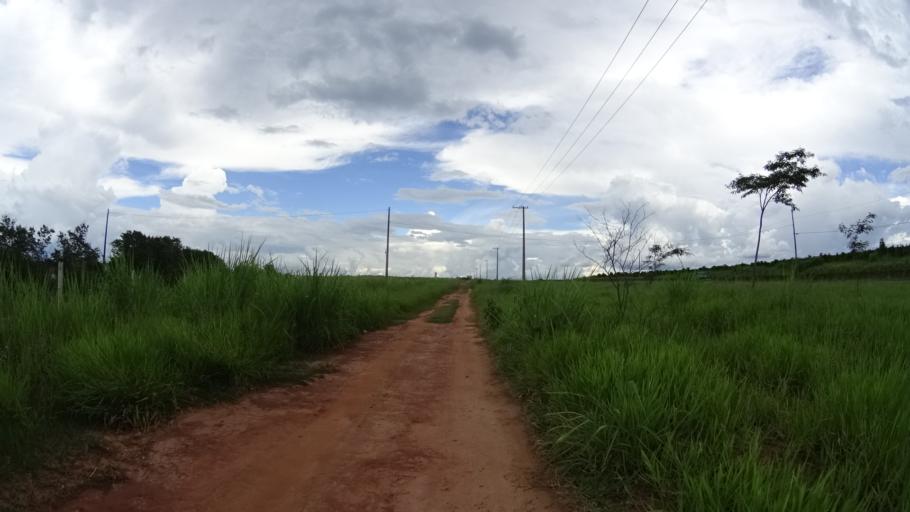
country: BR
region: Sao Paulo
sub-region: Marilia
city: Marilia
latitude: -22.2181
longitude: -49.8614
